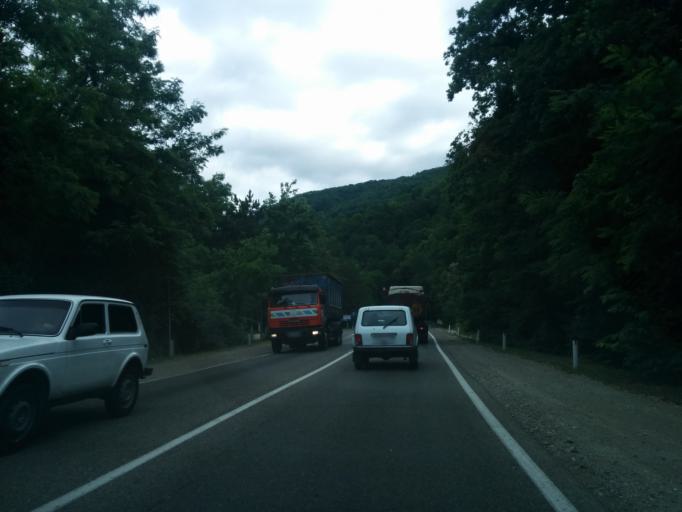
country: RU
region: Krasnodarskiy
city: Agoy
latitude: 44.1376
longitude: 39.0533
